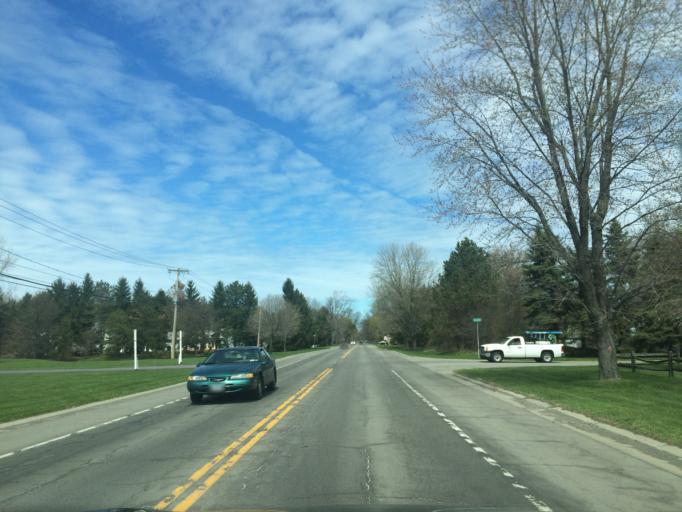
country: US
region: New York
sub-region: Monroe County
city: East Rochester
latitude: 43.0853
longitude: -77.4914
